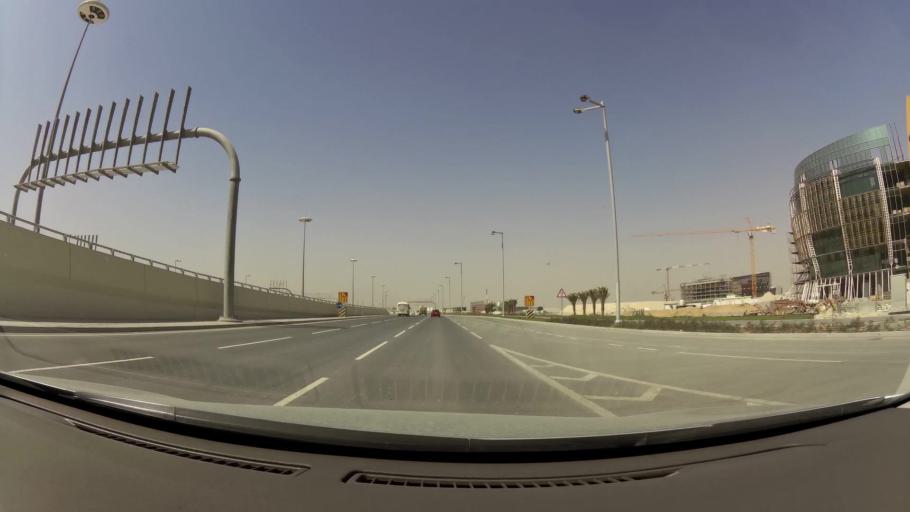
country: QA
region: Baladiyat Umm Salal
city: Umm Salal Muhammad
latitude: 25.3998
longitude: 51.5111
